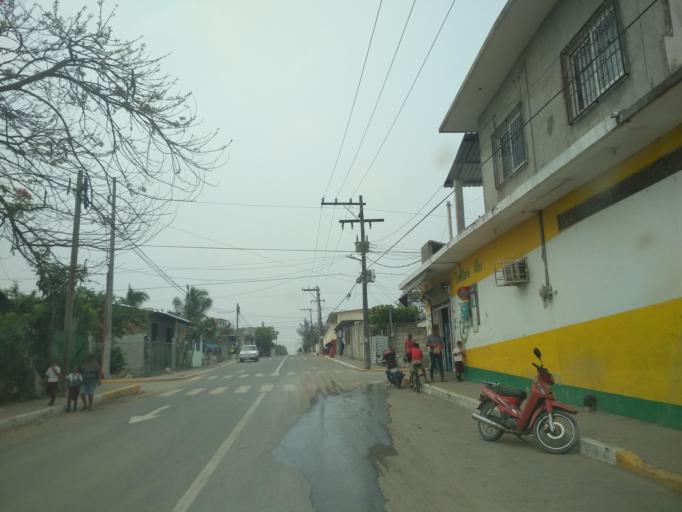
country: MX
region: Veracruz
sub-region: Veracruz
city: Rio Medio [Granja]
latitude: 19.2089
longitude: -96.2093
